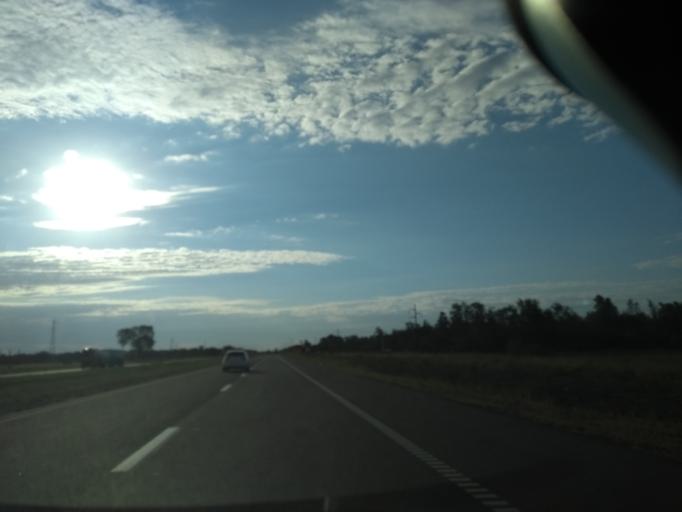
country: AR
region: Chaco
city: Puerto Tirol
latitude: -27.2739
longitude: -59.1401
